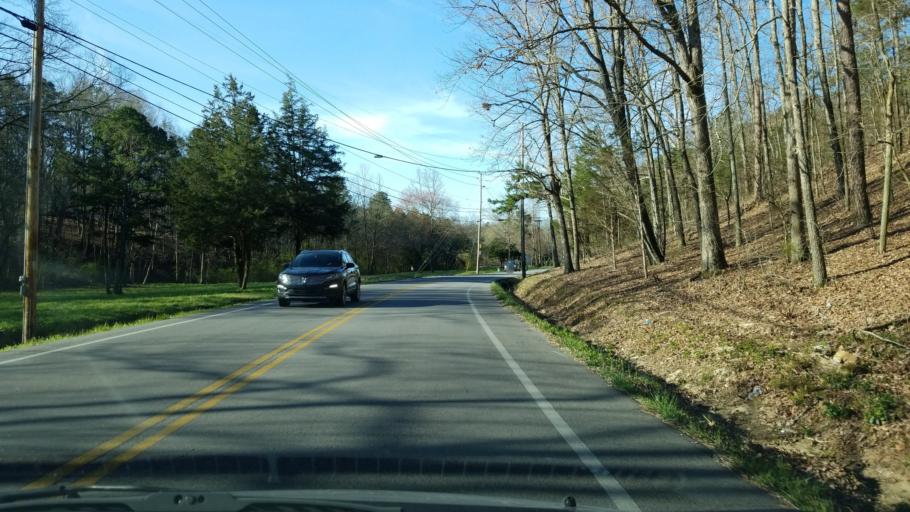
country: US
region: Tennessee
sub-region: Hamilton County
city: East Brainerd
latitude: 35.0151
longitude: -85.1123
